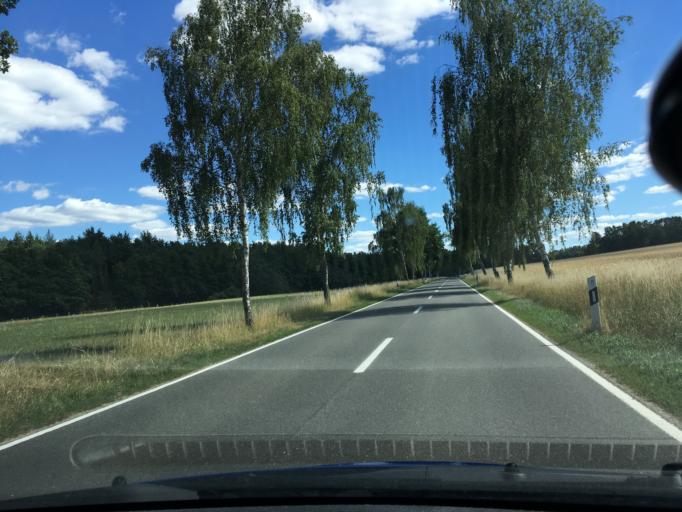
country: DE
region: Lower Saxony
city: Neu Darchau
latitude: 53.2035
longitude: 10.8767
